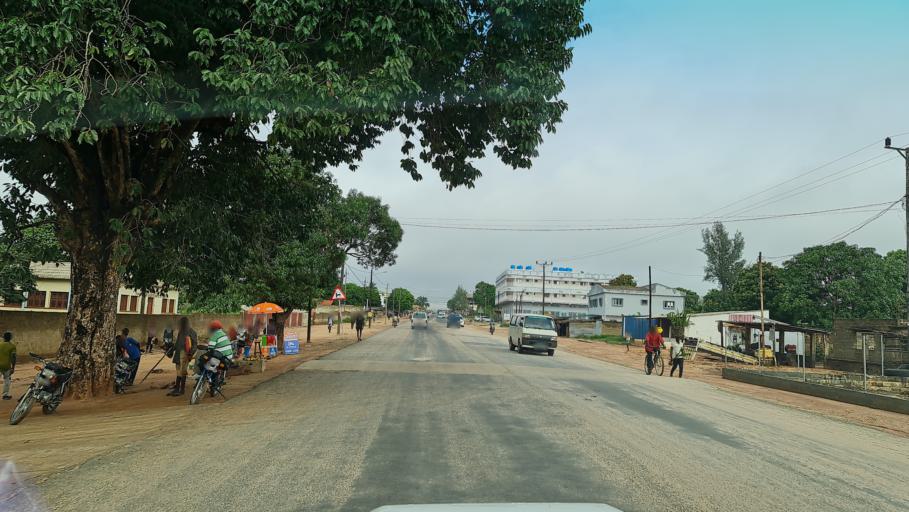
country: MZ
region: Nampula
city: Nampula
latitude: -15.1387
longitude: 39.2864
